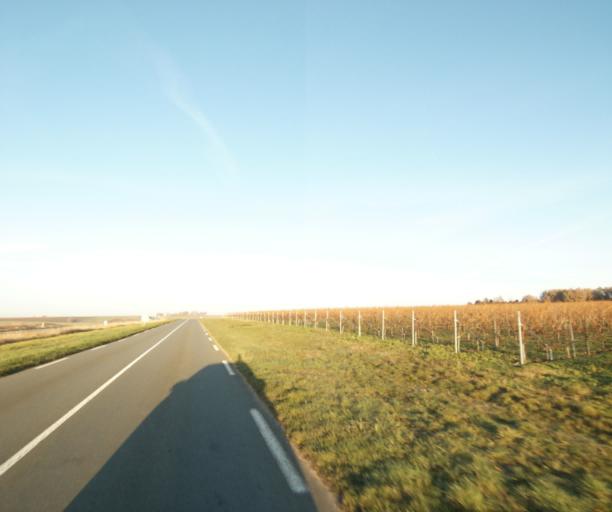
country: FR
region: Poitou-Charentes
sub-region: Departement de la Charente-Maritime
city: Cherac
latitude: 45.7042
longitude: -0.4740
